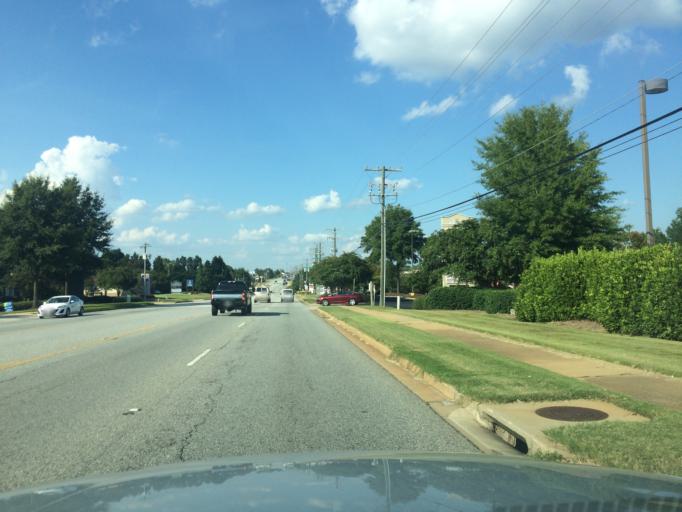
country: US
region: South Carolina
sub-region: Greenville County
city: Simpsonville
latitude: 34.7114
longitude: -82.2564
